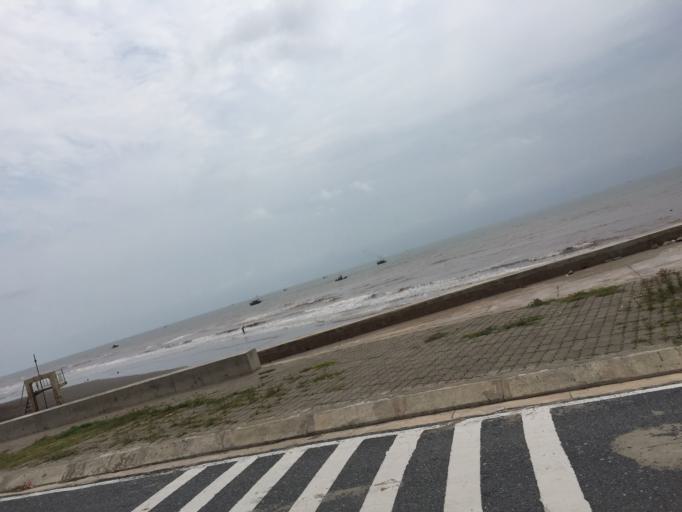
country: VN
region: Ninh Binh
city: Thi Tran Phat Diem
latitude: 20.0346
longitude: 106.2271
